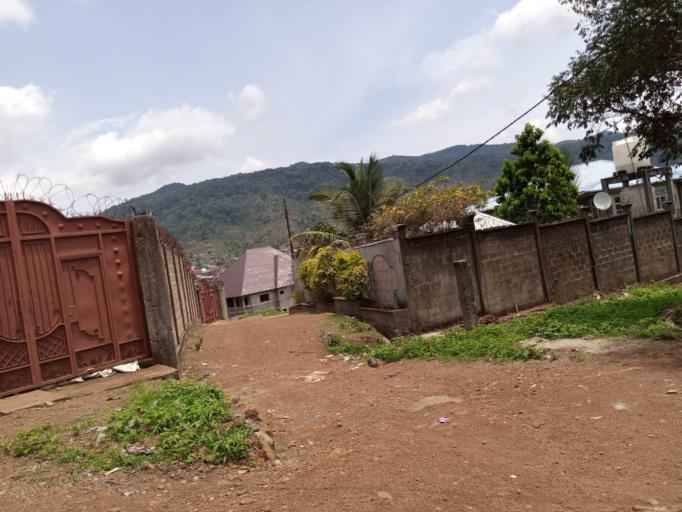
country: SL
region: Western Area
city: Hastings
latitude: 8.3801
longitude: -13.1475
